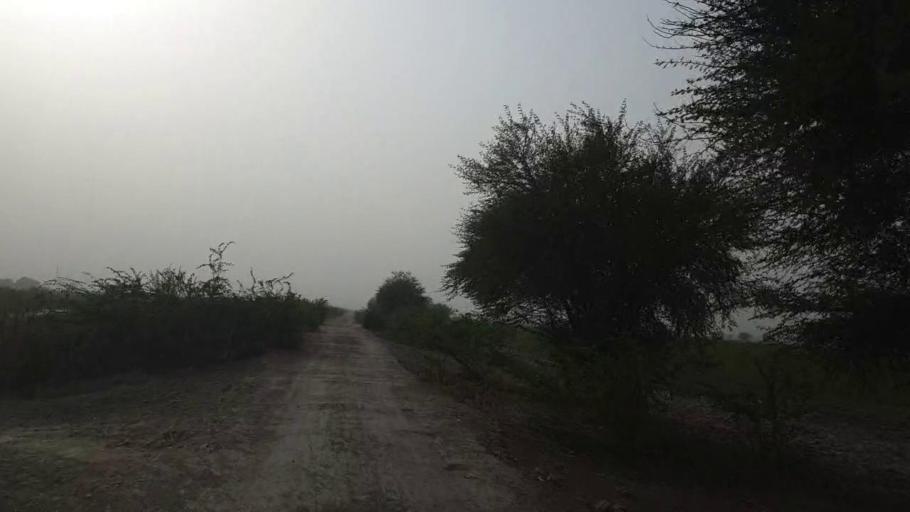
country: PK
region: Sindh
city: Kunri
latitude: 25.0672
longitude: 69.4791
